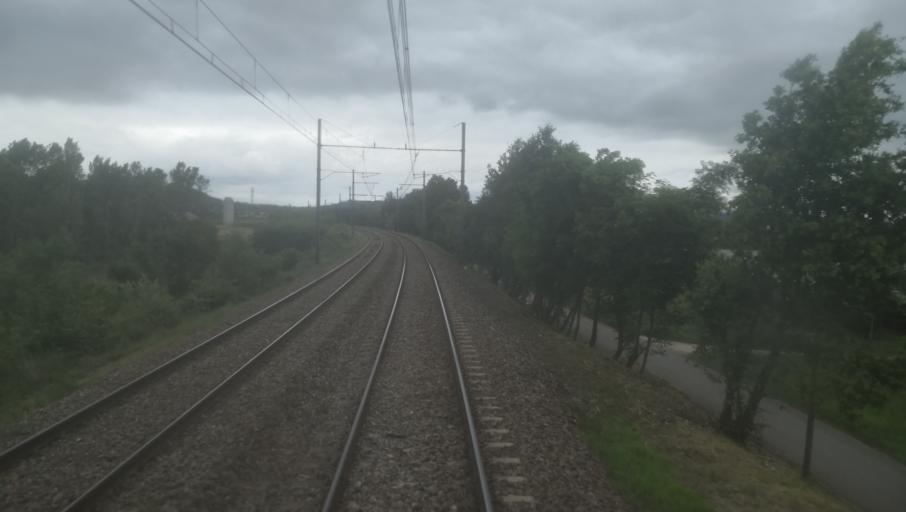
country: FR
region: Midi-Pyrenees
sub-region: Departement du Tarn-et-Garonne
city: Moissac
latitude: 44.0958
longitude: 1.1062
